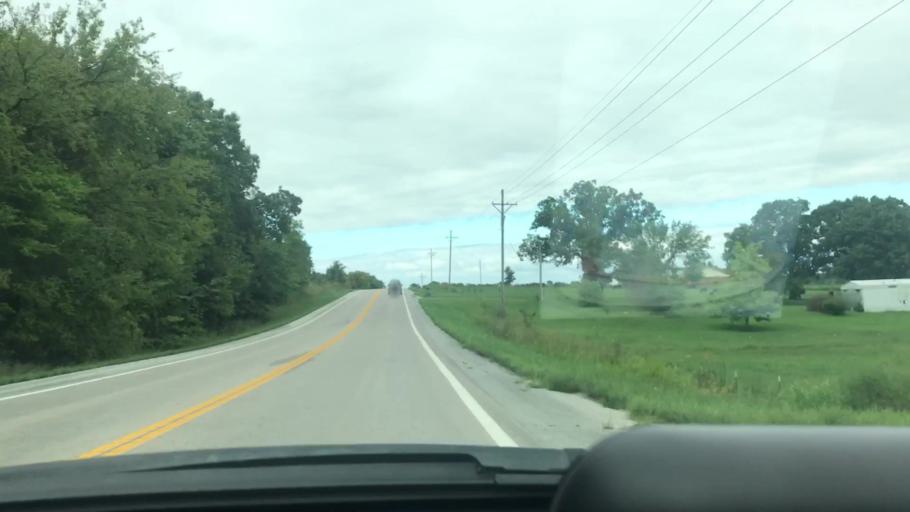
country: US
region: Missouri
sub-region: Hickory County
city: Hermitage
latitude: 37.8719
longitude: -93.1807
